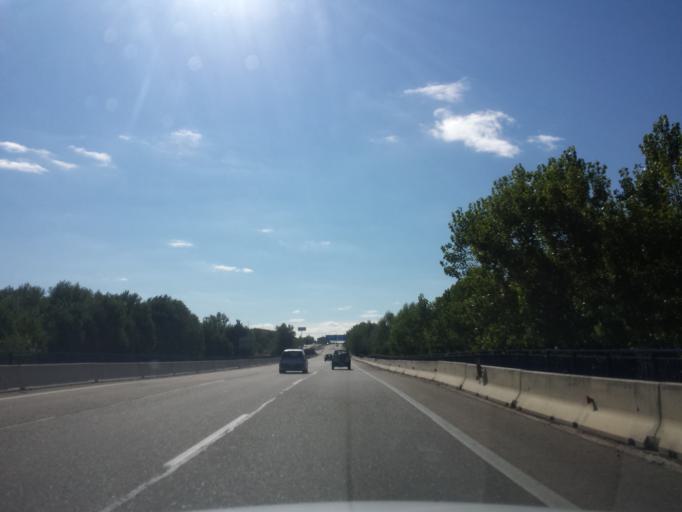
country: ES
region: Castille and Leon
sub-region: Provincia de Zamora
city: Castrogonzalo
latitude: 41.9837
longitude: -5.6249
